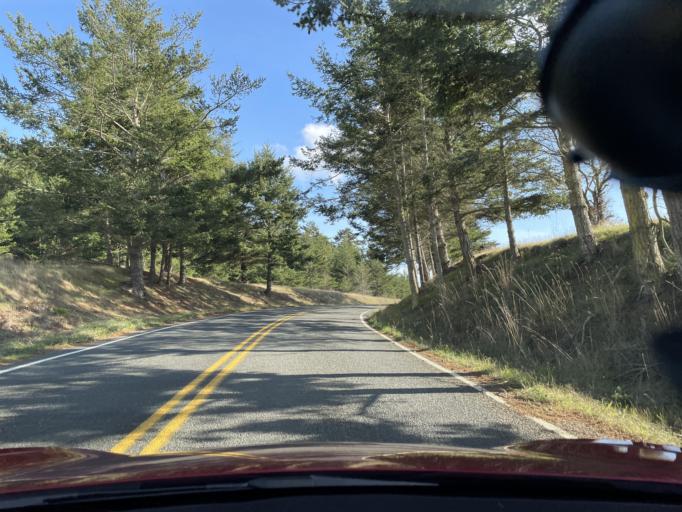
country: US
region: Washington
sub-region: San Juan County
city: Friday Harbor
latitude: 48.4632
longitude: -122.9990
